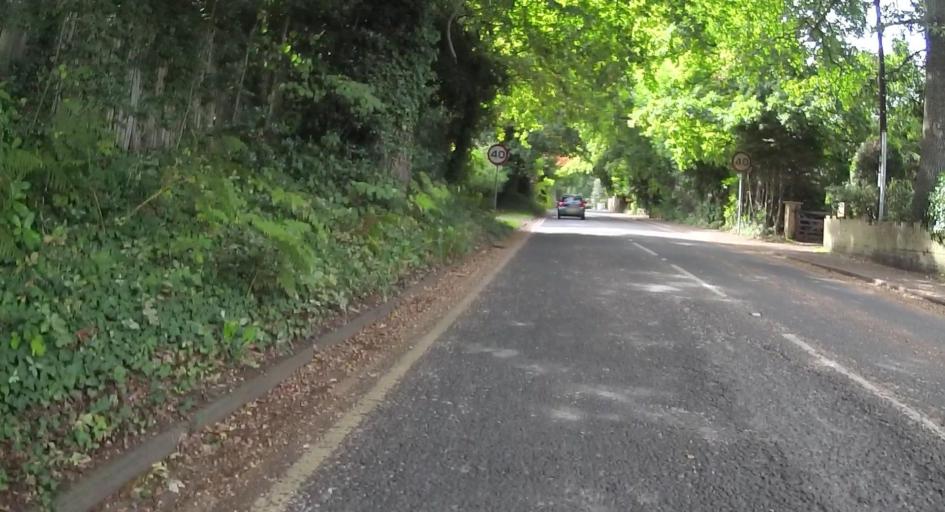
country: GB
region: England
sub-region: Surrey
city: Windlesham
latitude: 51.3489
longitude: -0.6628
